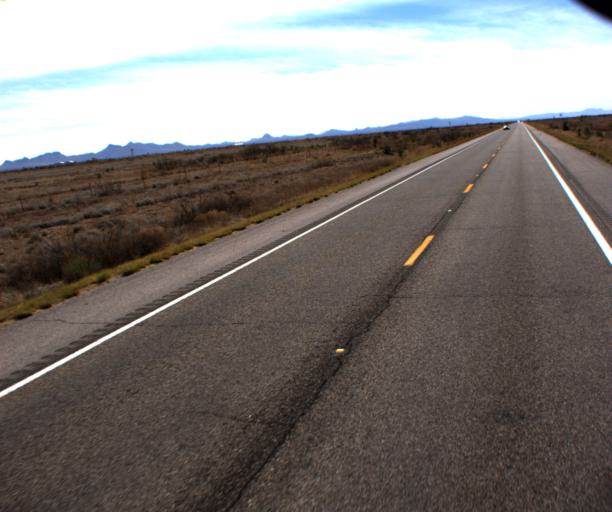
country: US
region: Arizona
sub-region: Cochise County
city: Pirtleville
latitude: 31.4774
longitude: -109.6227
